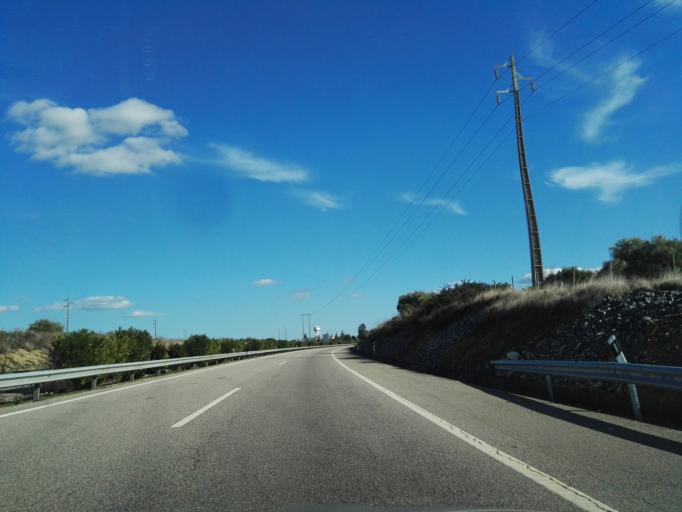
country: PT
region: Santarem
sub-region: Alcanena
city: Alcanena
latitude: 39.4788
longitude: -8.6133
